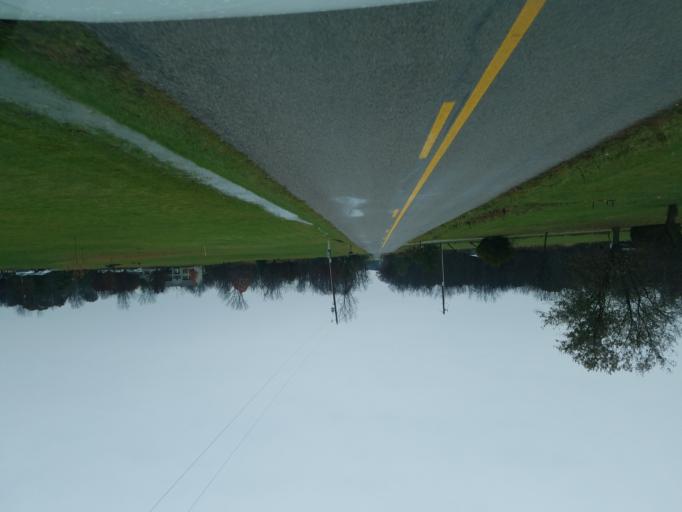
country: US
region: Ohio
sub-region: Knox County
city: Centerburg
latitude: 40.3438
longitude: -82.7751
